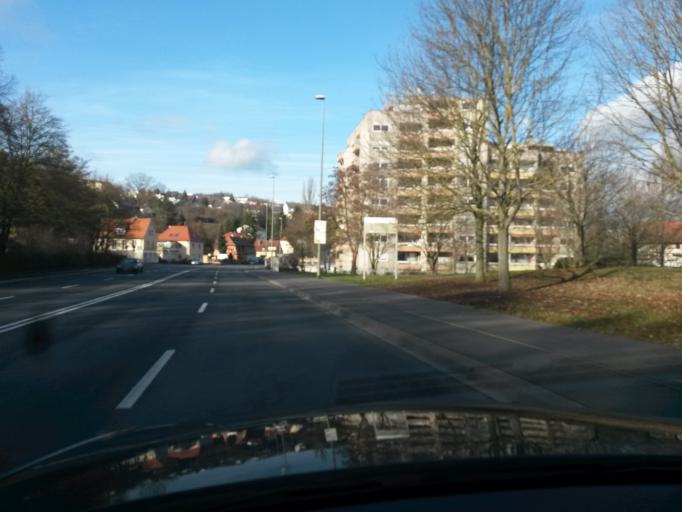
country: DE
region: Bavaria
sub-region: Regierungsbezirk Unterfranken
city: Wuerzburg
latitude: 49.8130
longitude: 9.9634
